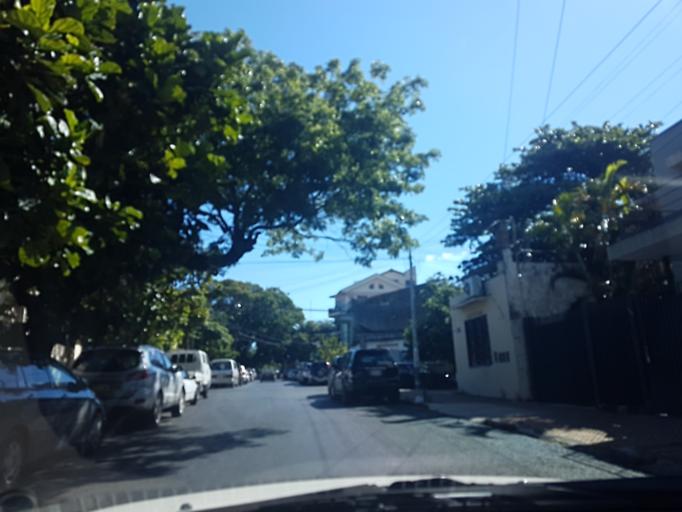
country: PY
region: Asuncion
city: Asuncion
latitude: -25.2943
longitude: -57.6343
